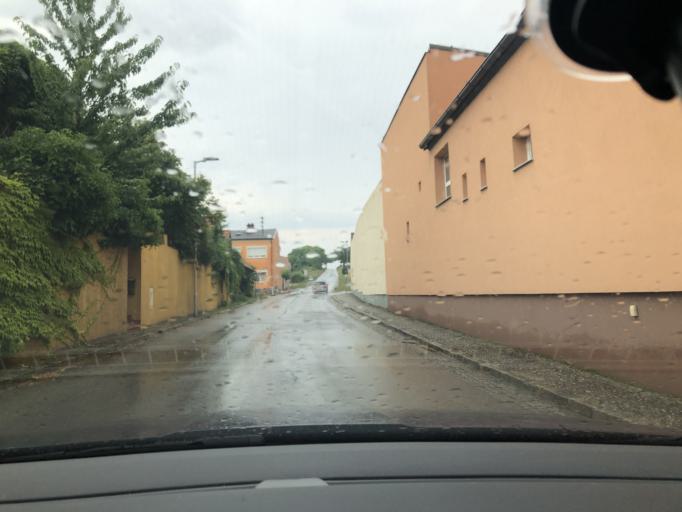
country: AT
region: Lower Austria
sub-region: Politischer Bezirk Ganserndorf
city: Auersthal
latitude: 48.3734
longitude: 16.6414
